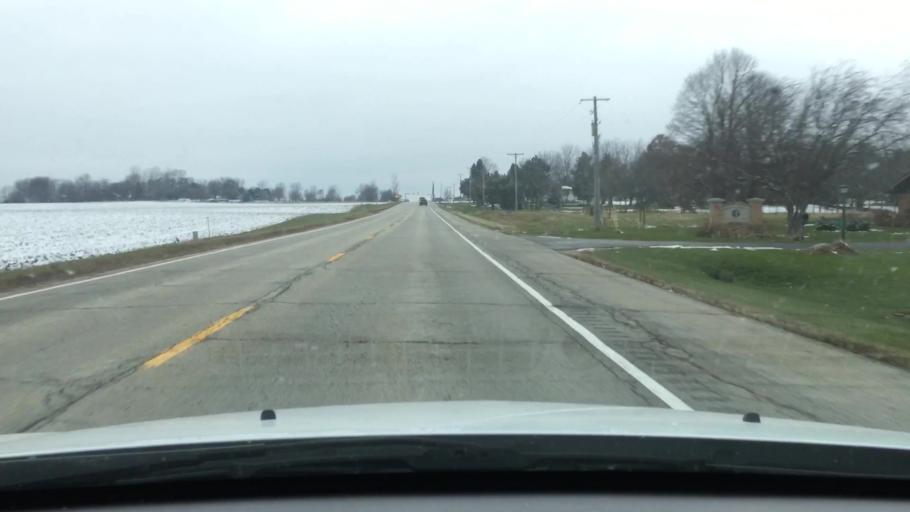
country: US
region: Illinois
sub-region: DeKalb County
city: Malta
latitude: 41.9357
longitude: -88.8684
